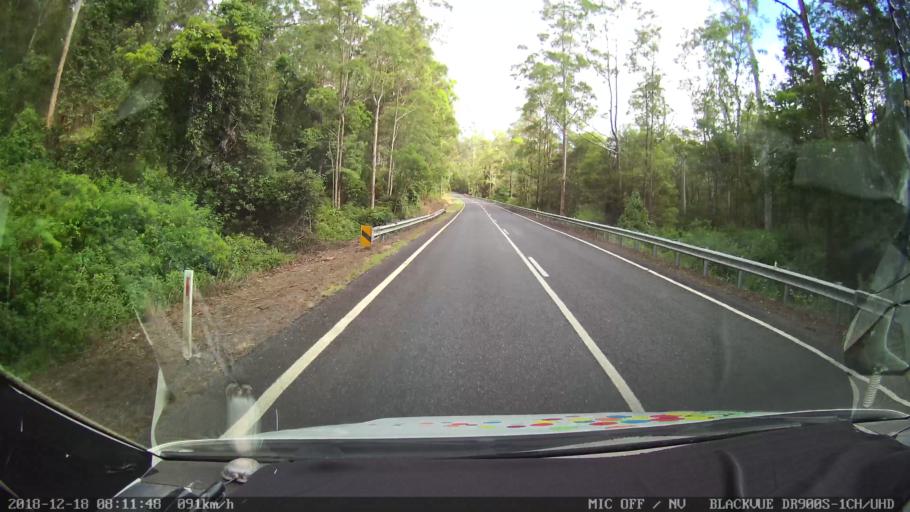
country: AU
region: New South Wales
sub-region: Kyogle
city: Kyogle
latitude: -28.3461
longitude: 152.6701
